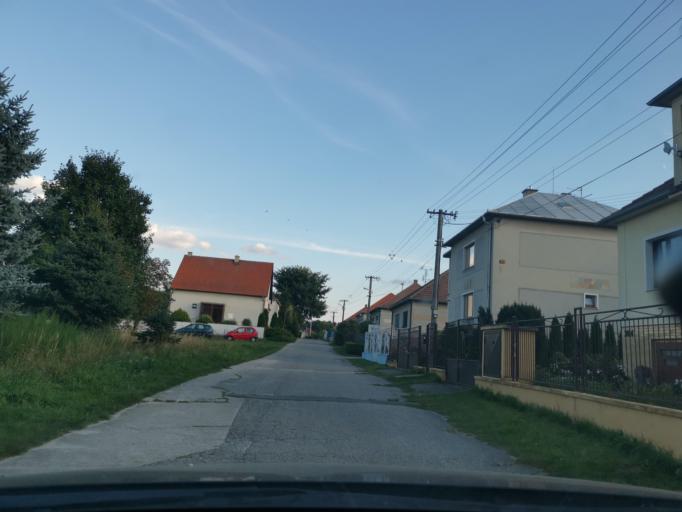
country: SK
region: Trnavsky
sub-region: Okres Senica
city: Senica
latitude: 48.6538
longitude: 17.2661
